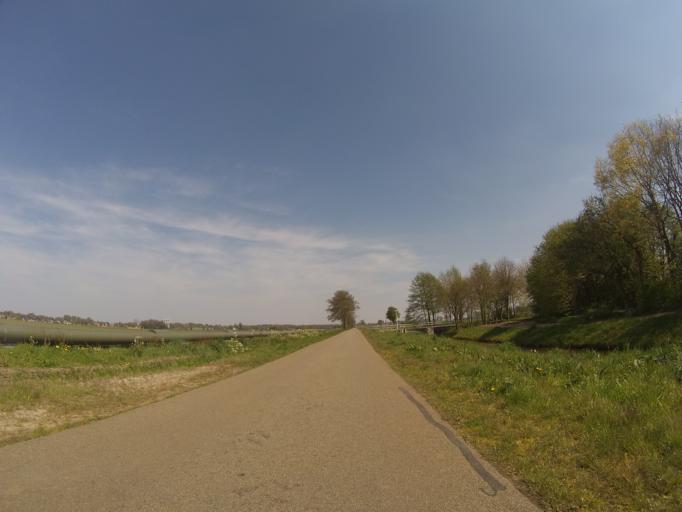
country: NL
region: Drenthe
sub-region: Gemeente Emmen
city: Schoonebeek
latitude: 52.6511
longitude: 6.8852
